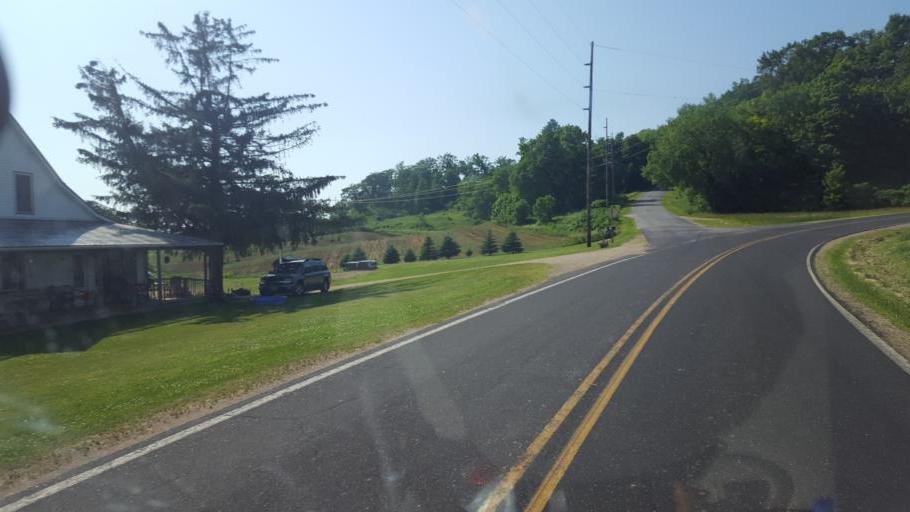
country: US
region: Wisconsin
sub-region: Vernon County
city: Hillsboro
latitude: 43.6679
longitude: -90.3514
